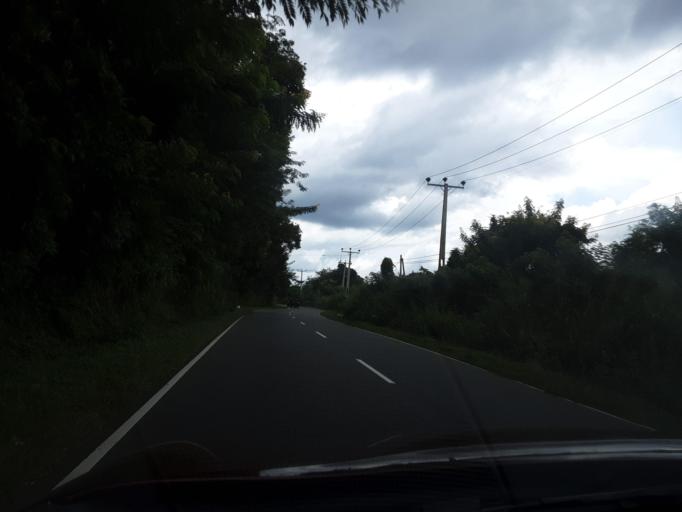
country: LK
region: Uva
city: Monaragala
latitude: 6.9027
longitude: 81.2118
